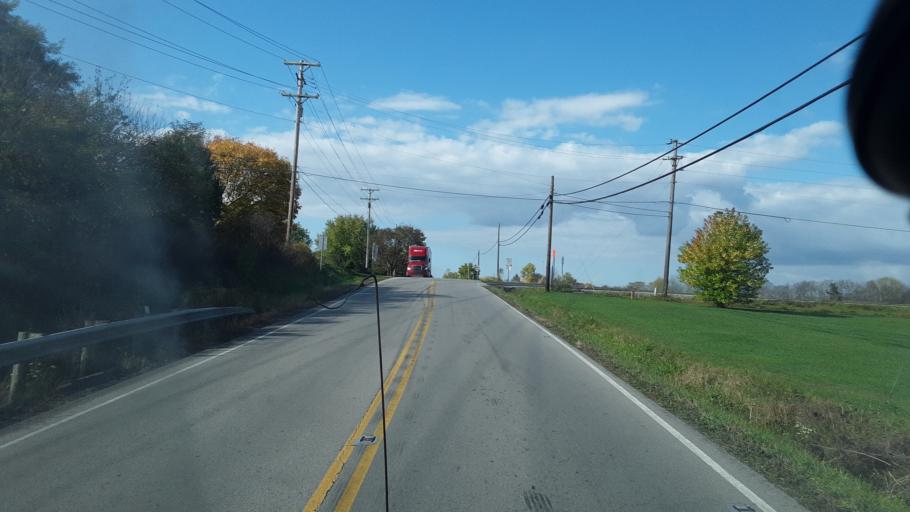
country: US
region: Ohio
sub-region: Highland County
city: Leesburg
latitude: 39.3472
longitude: -83.5871
